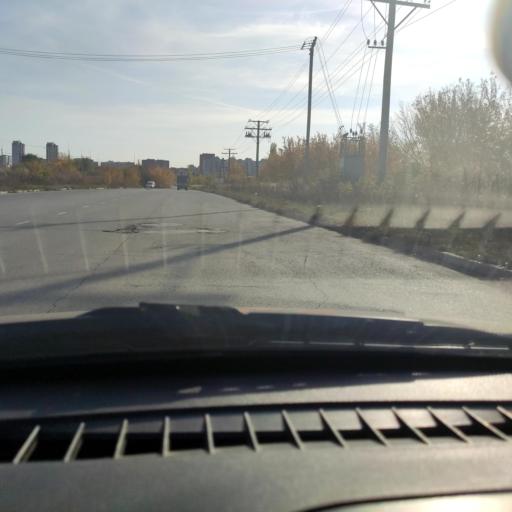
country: RU
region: Samara
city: Tol'yatti
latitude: 53.5553
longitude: 49.3289
